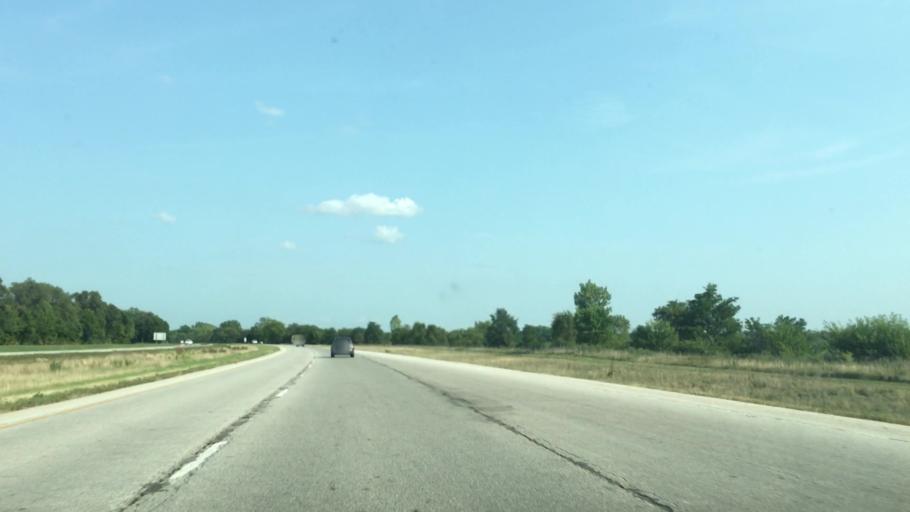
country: US
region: Illinois
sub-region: Rock Island County
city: Milan
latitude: 41.4601
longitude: -90.6109
